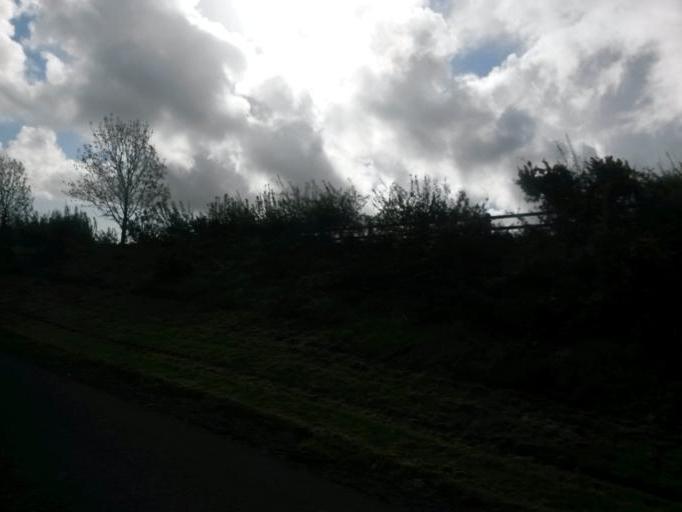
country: IE
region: Leinster
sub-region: Loch Garman
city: Gorey
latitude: 52.6489
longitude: -6.3205
